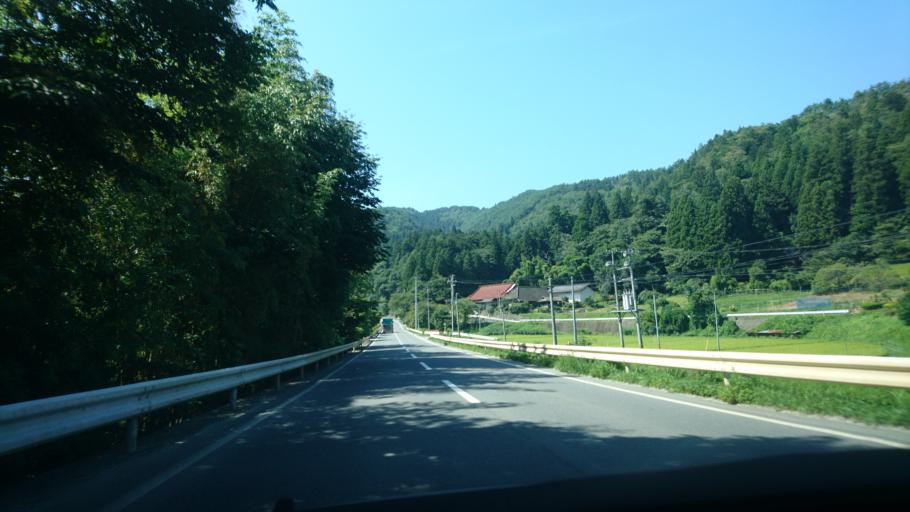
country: JP
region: Iwate
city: Ofunato
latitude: 39.0227
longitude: 141.5726
